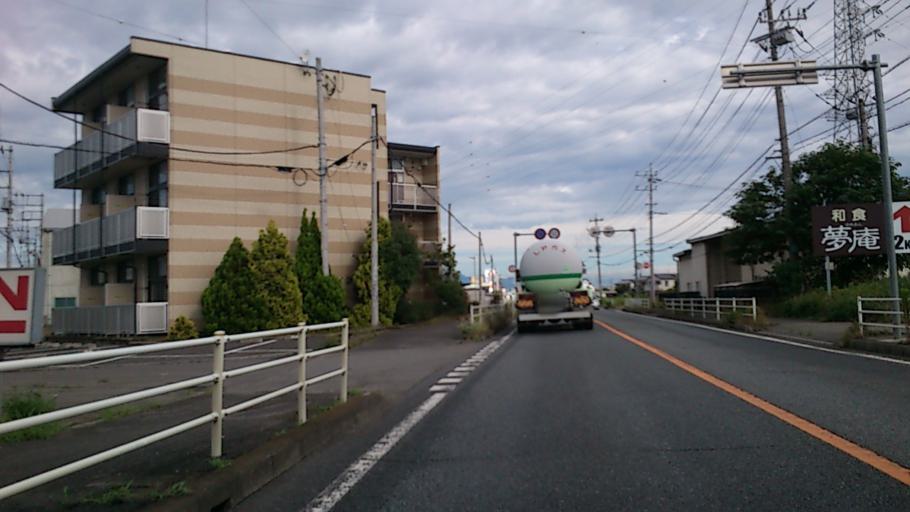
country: JP
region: Saitama
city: Honjo
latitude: 36.2370
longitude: 139.2067
